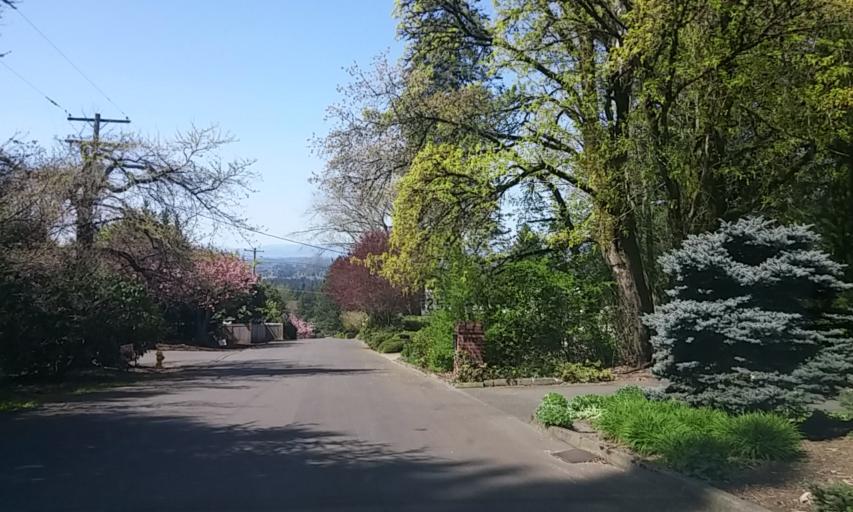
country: US
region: Oregon
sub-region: Washington County
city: West Haven-Sylvan
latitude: 45.5196
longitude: -122.7642
